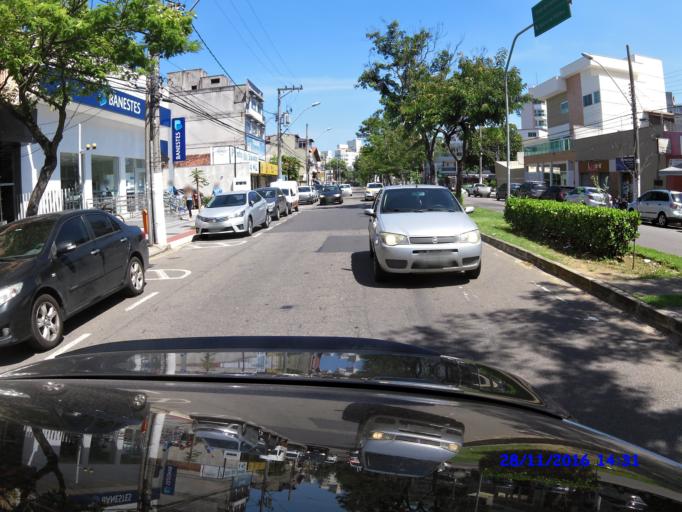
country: BR
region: Espirito Santo
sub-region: Vila Velha
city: Vila Velha
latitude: -20.2581
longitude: -40.2659
